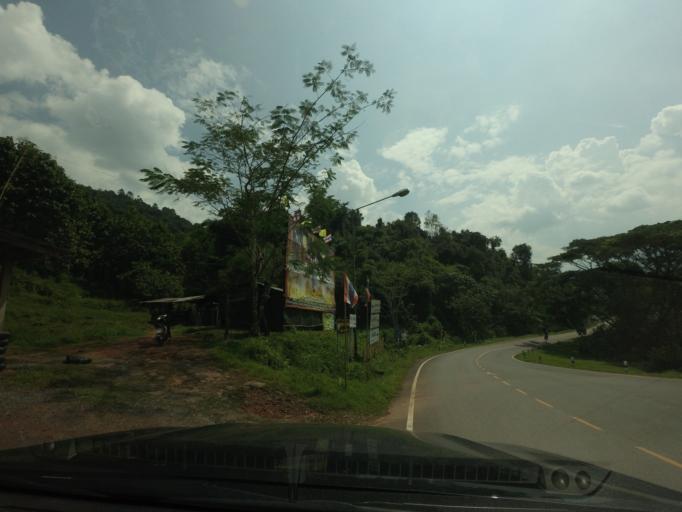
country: TH
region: Nan
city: Bo Kluea
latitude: 19.1520
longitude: 101.1576
